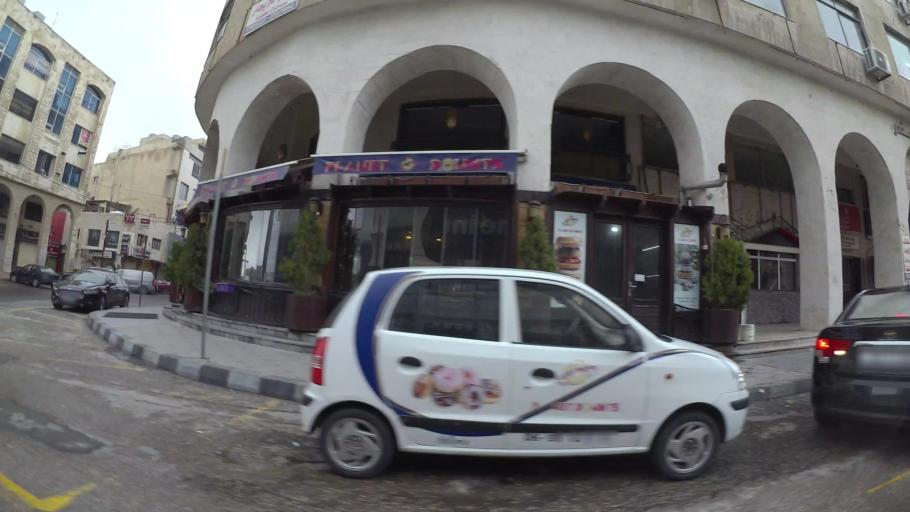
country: JO
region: Amman
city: Wadi as Sir
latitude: 31.9574
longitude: 35.8688
